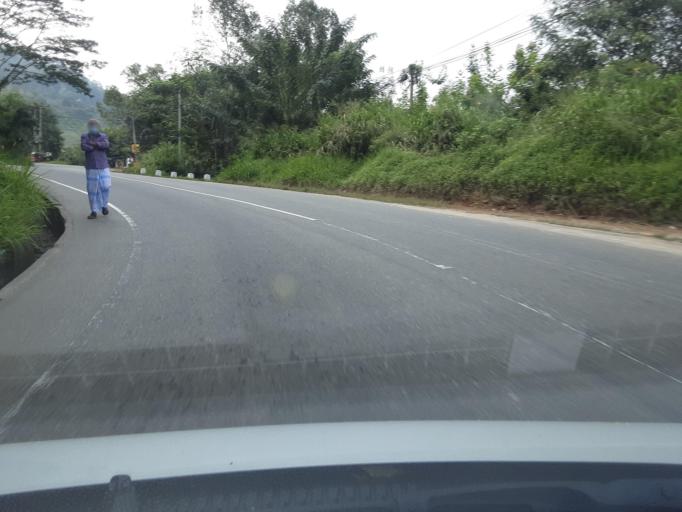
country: LK
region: Uva
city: Badulla
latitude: 6.9533
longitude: 81.0234
